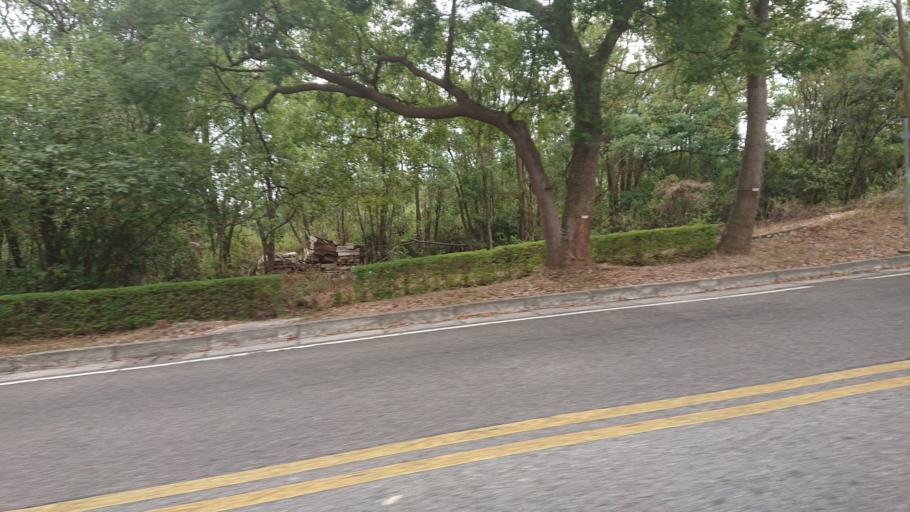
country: TW
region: Fukien
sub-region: Kinmen
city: Jincheng
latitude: 24.4264
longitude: 118.3210
